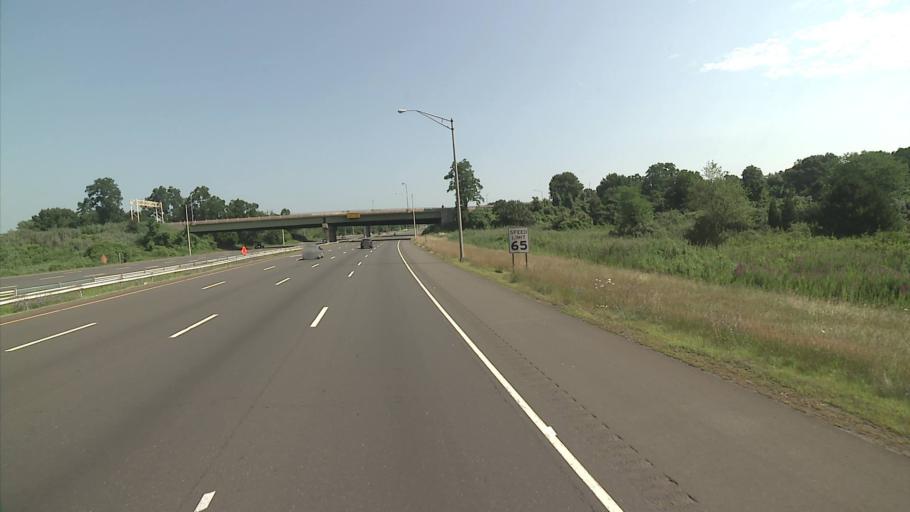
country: US
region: Connecticut
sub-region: New Haven County
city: North Haven
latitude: 41.3747
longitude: -72.8691
